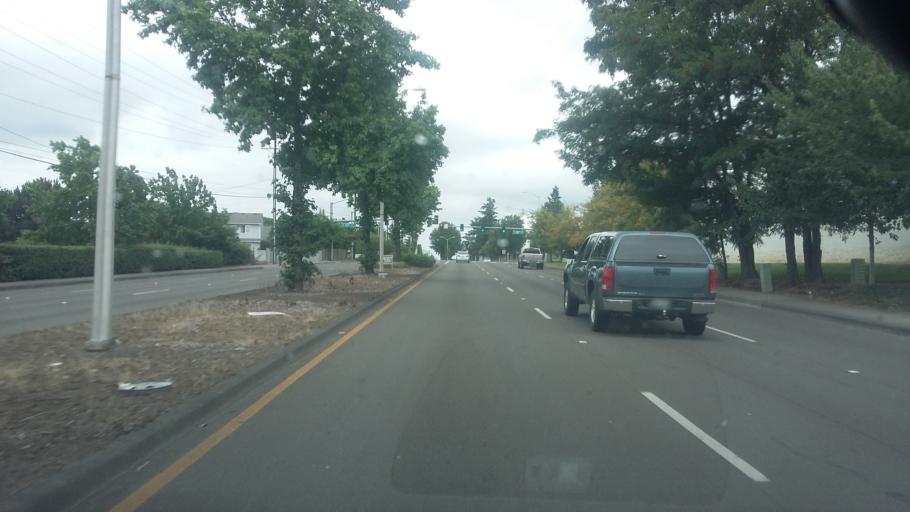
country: US
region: Washington
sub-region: Clark County
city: Mill Plain
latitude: 45.6165
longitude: -122.5128
